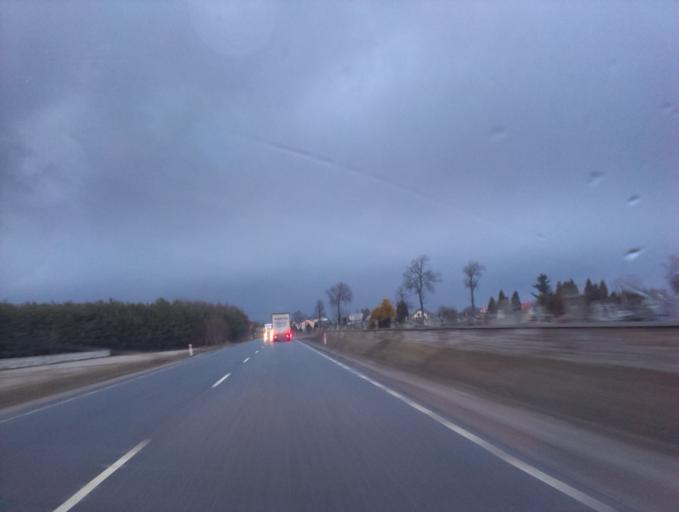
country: PL
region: Lodz Voivodeship
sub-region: Powiat opoczynski
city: Zarnow
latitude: 51.2399
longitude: 20.1764
